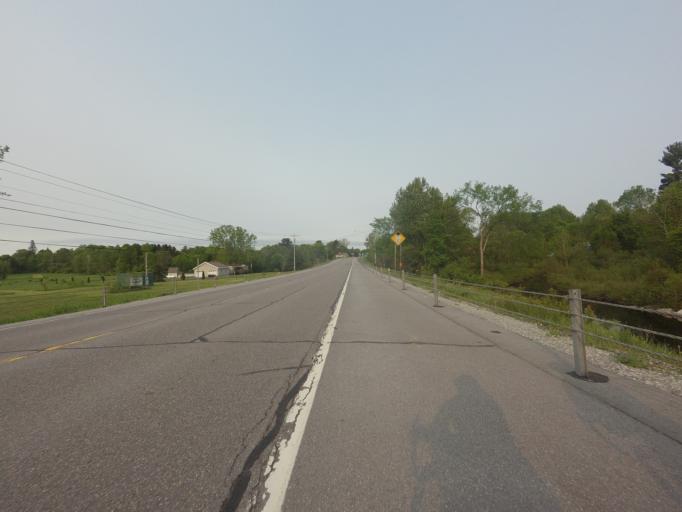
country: US
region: New York
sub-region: Jefferson County
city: Carthage
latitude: 44.0702
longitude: -75.4877
